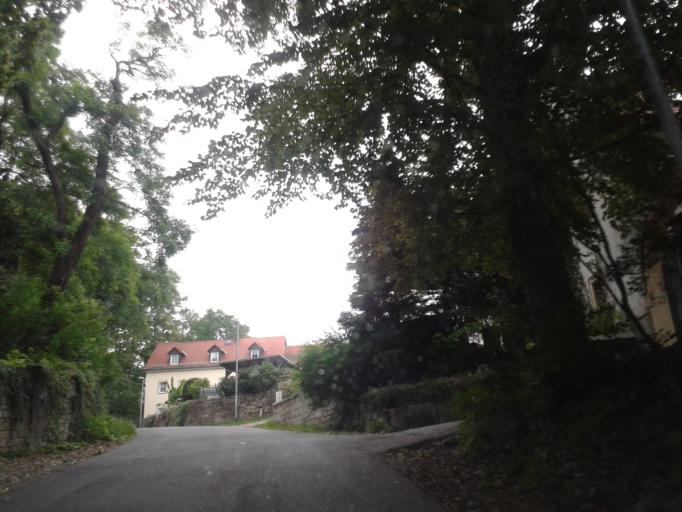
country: DE
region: Saxony
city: Bannewitz
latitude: 51.0045
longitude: 13.7316
